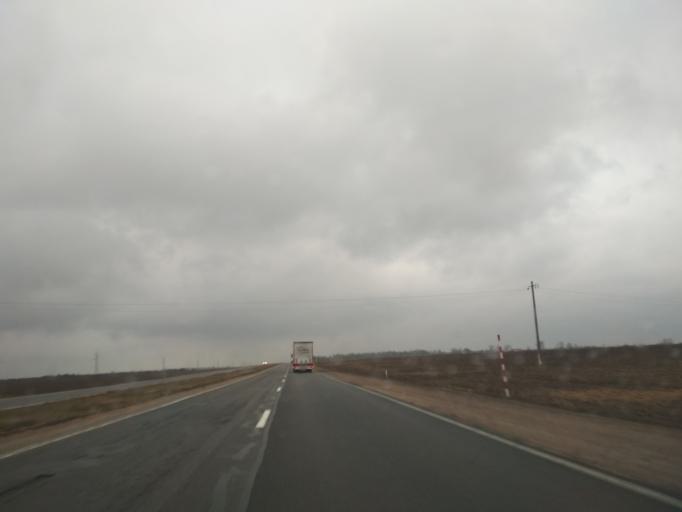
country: BY
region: Minsk
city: Dukora
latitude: 53.6423
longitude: 27.9932
